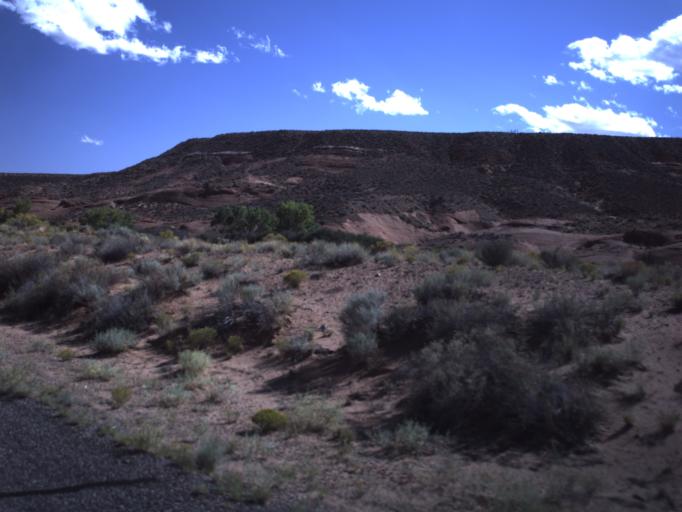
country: US
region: Utah
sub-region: Wayne County
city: Loa
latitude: 38.0592
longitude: -110.5952
